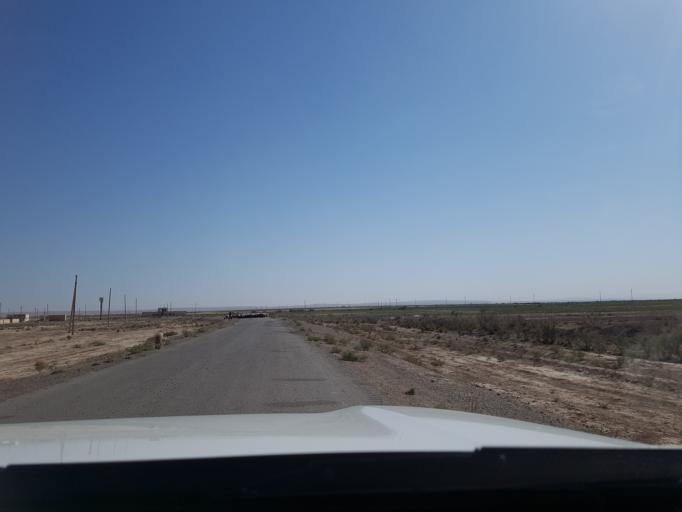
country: IR
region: Razavi Khorasan
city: Sarakhs
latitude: 36.4959
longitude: 61.2537
